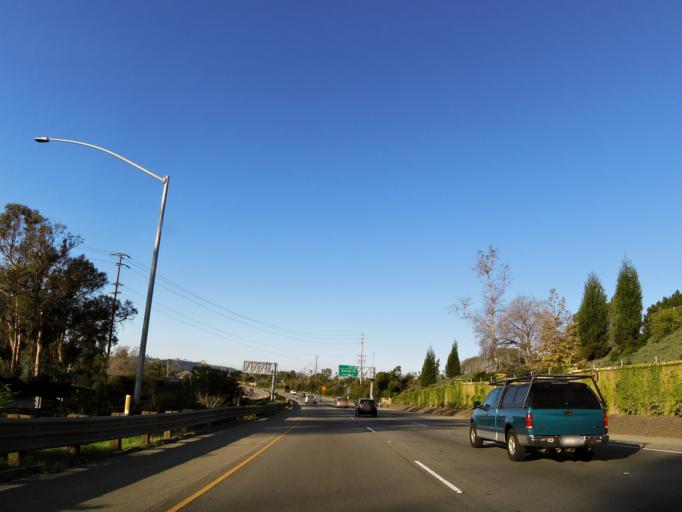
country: US
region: California
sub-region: Santa Barbara County
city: Montecito
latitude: 34.4232
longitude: -119.6576
